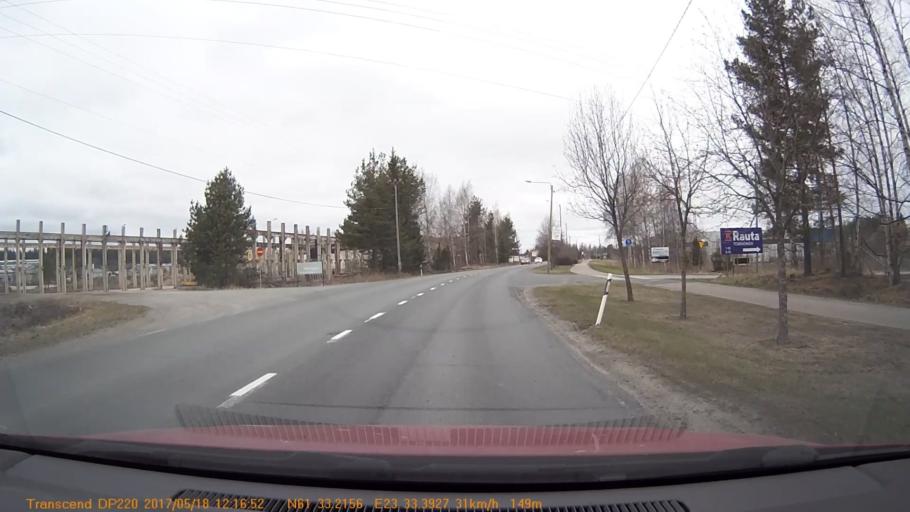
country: FI
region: Pirkanmaa
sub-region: Tampere
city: Yloejaervi
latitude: 61.5535
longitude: 23.5568
